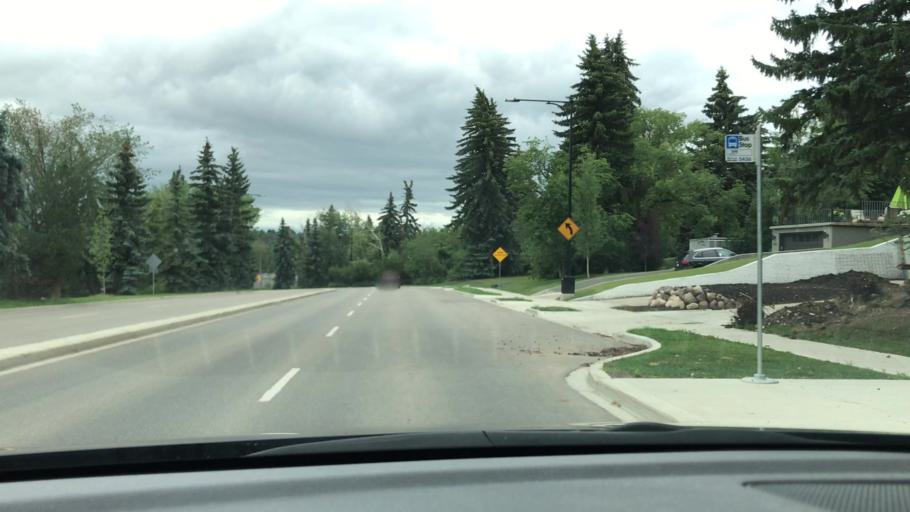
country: CA
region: Alberta
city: Edmonton
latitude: 53.5150
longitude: -113.5561
